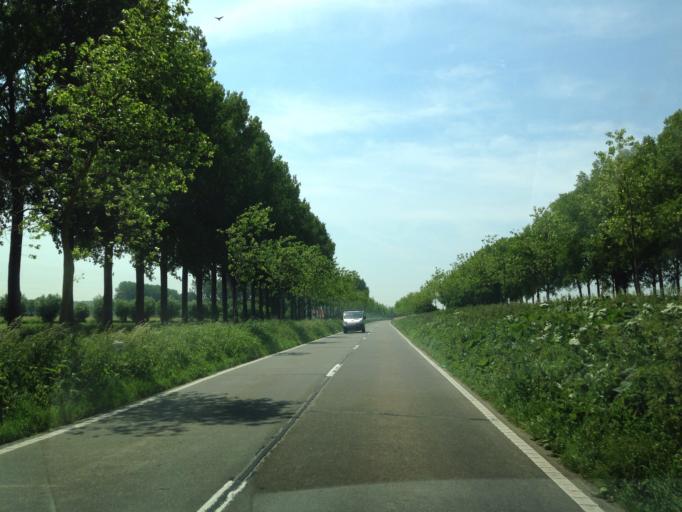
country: BE
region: Flanders
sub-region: Provincie West-Vlaanderen
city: Damme
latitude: 51.2375
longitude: 3.2634
